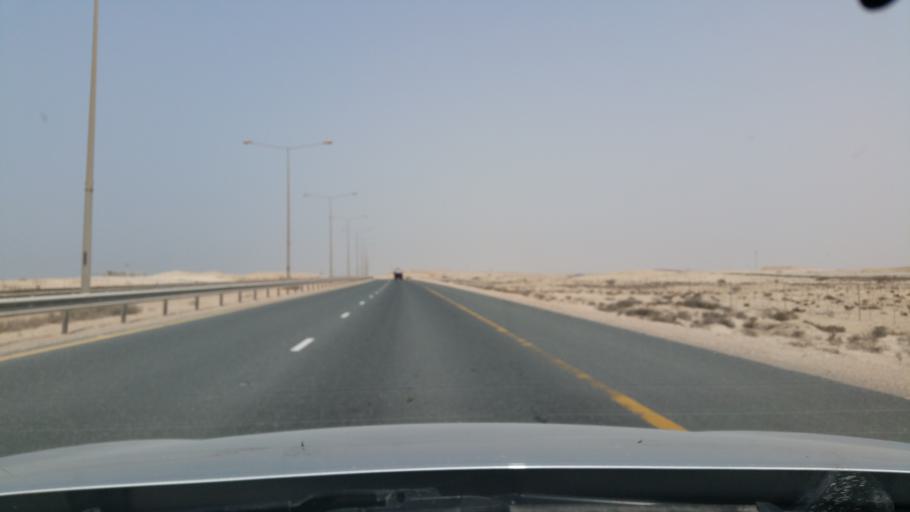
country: QA
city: Umm Bab
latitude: 25.2427
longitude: 50.8007
